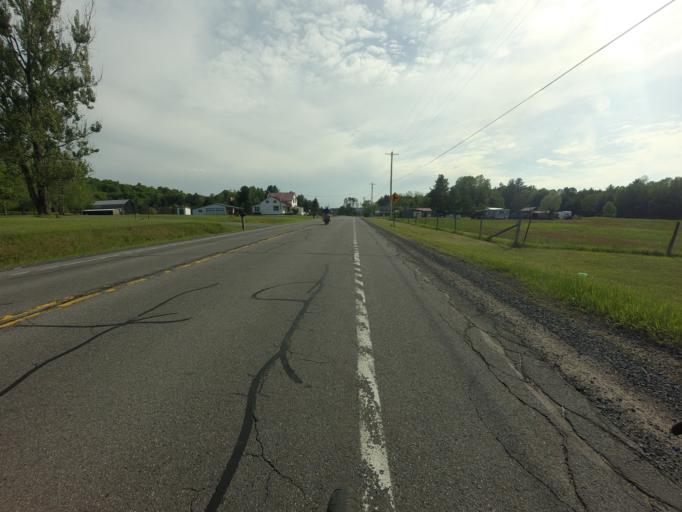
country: US
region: New York
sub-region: St. Lawrence County
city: Gouverneur
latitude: 44.1748
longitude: -75.2941
